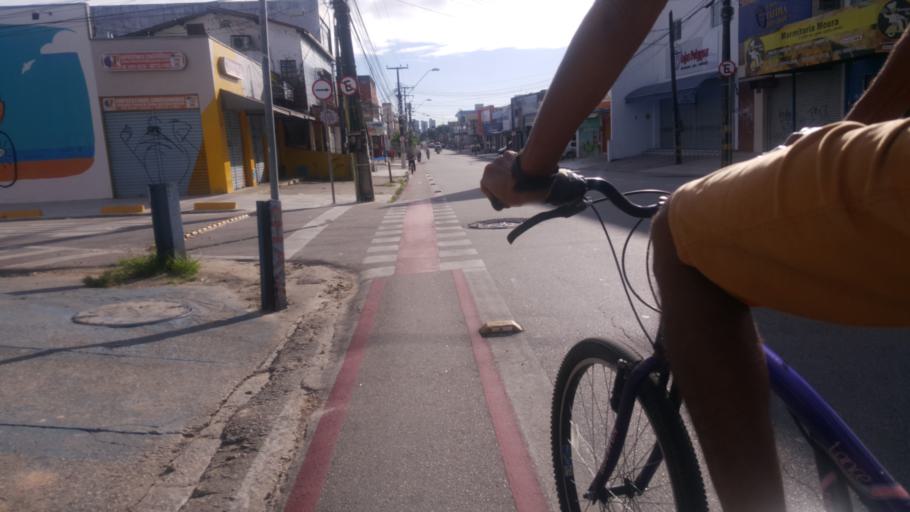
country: BR
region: Ceara
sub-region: Fortaleza
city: Fortaleza
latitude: -3.7602
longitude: -38.5442
